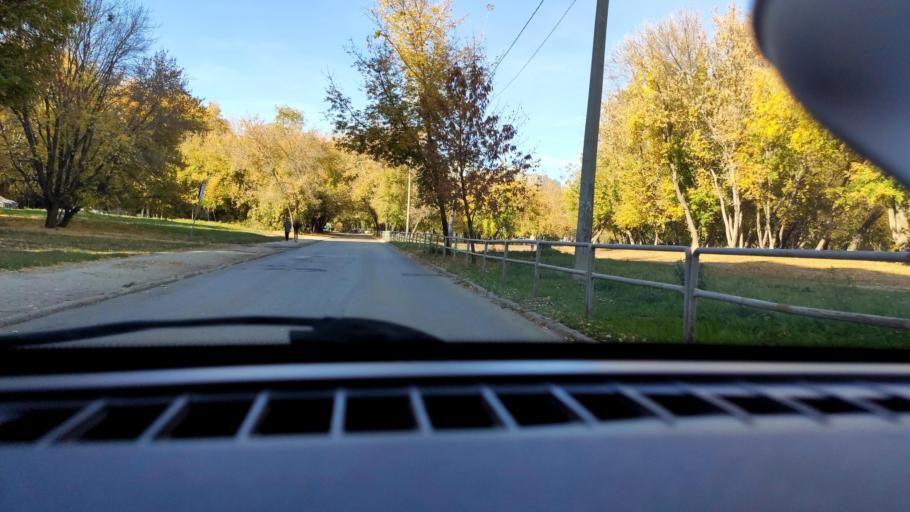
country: RU
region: Samara
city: Samara
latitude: 53.2414
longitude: 50.2224
